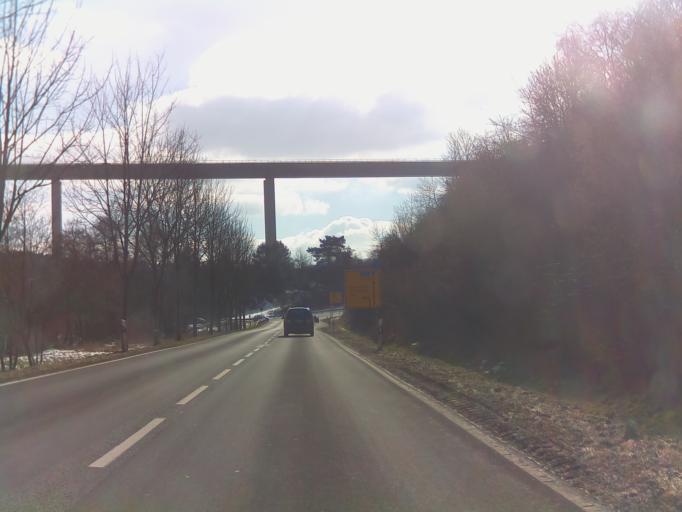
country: DE
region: Thuringia
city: Schwarza
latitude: 50.6019
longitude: 10.5213
